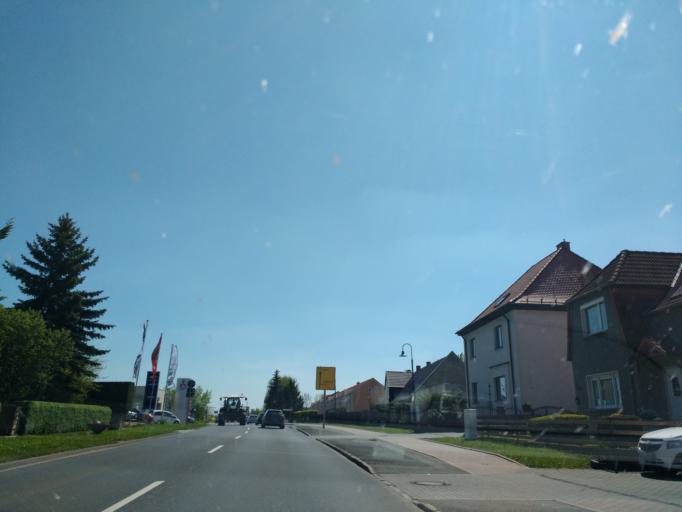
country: DE
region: Saxony-Anhalt
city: Theissen
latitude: 51.0846
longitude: 12.1095
